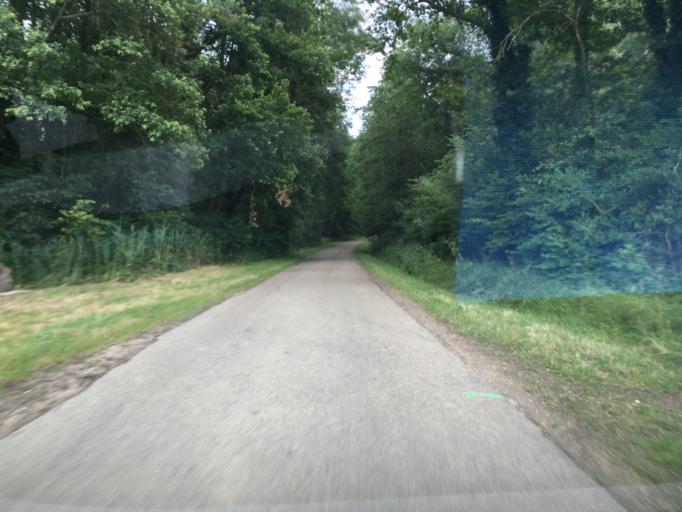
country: FR
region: Bourgogne
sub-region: Departement de l'Yonne
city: Charbuy
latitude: 47.8271
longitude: 3.4134
